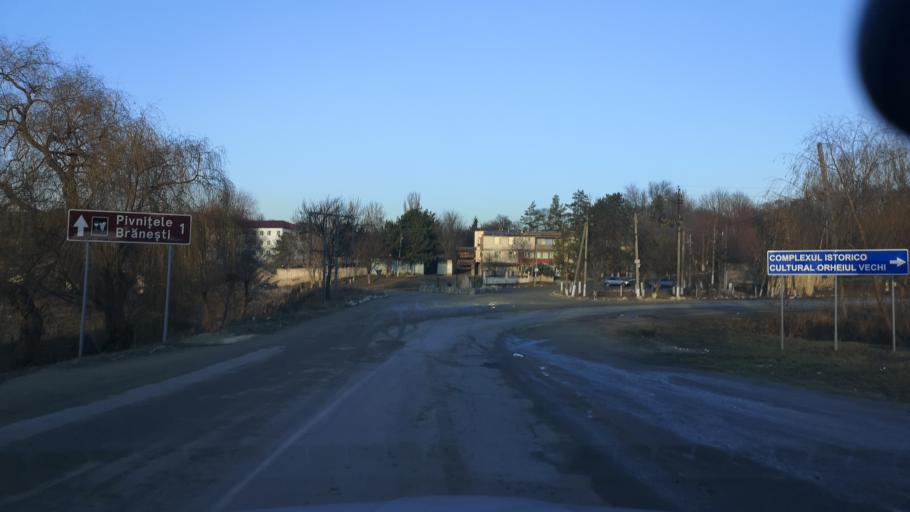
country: MD
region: Orhei
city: Orhei
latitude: 47.3093
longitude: 28.9314
